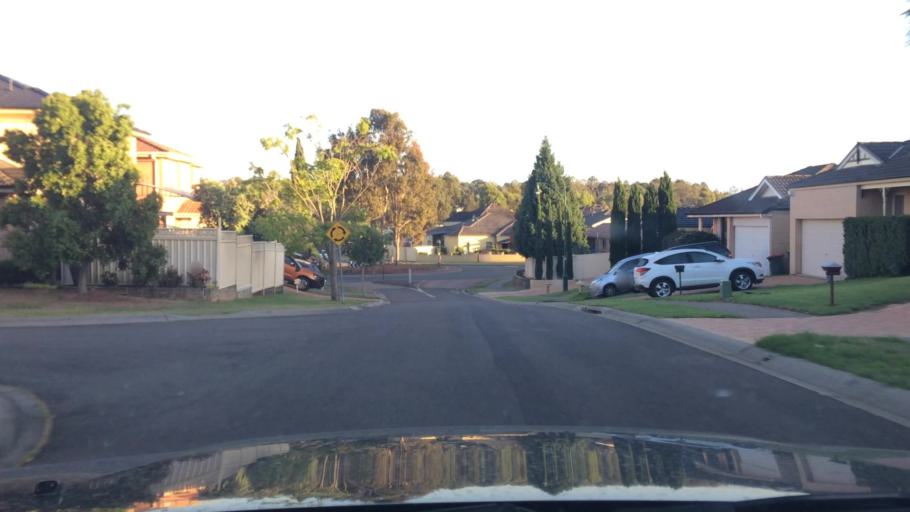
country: AU
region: New South Wales
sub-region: Campbelltown Municipality
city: Denham Court
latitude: -33.9368
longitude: 150.8336
